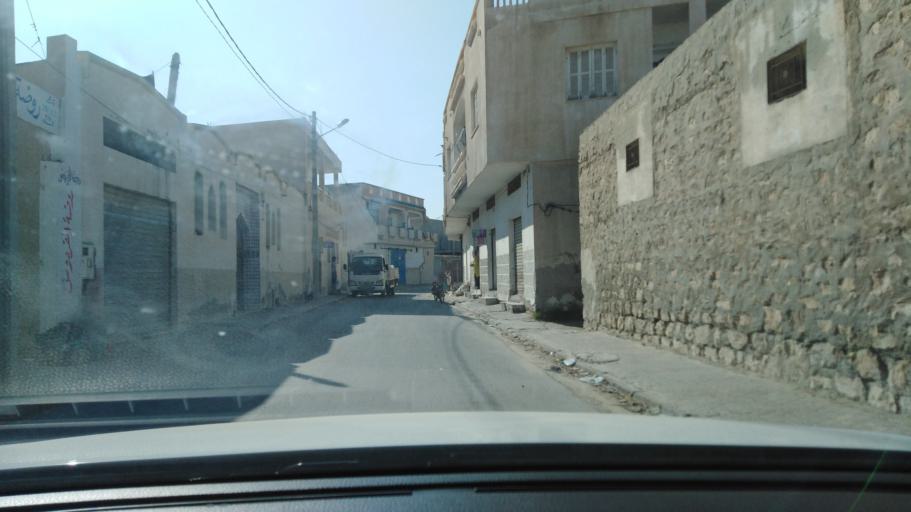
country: TN
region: Qabis
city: Gabes
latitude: 33.9382
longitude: 10.0639
